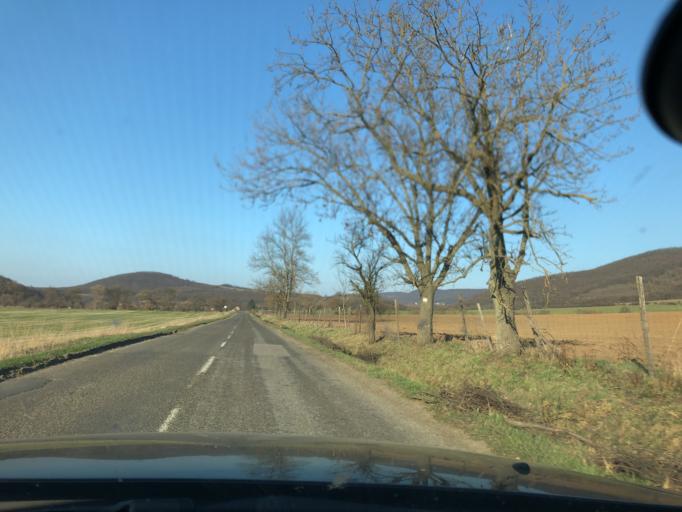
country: HU
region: Nograd
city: Bujak
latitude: 47.9592
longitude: 19.5989
